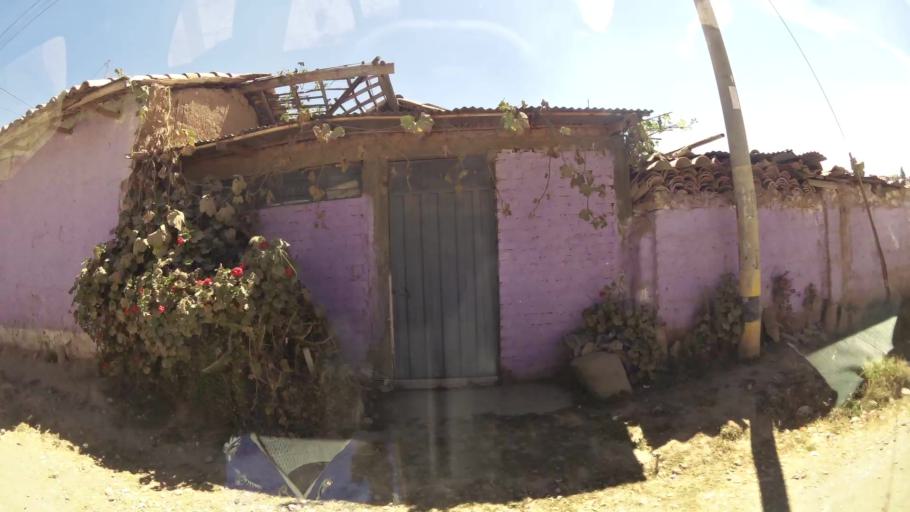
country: PE
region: Junin
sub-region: Provincia de Jauja
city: Jauja
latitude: -11.7741
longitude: -75.4934
